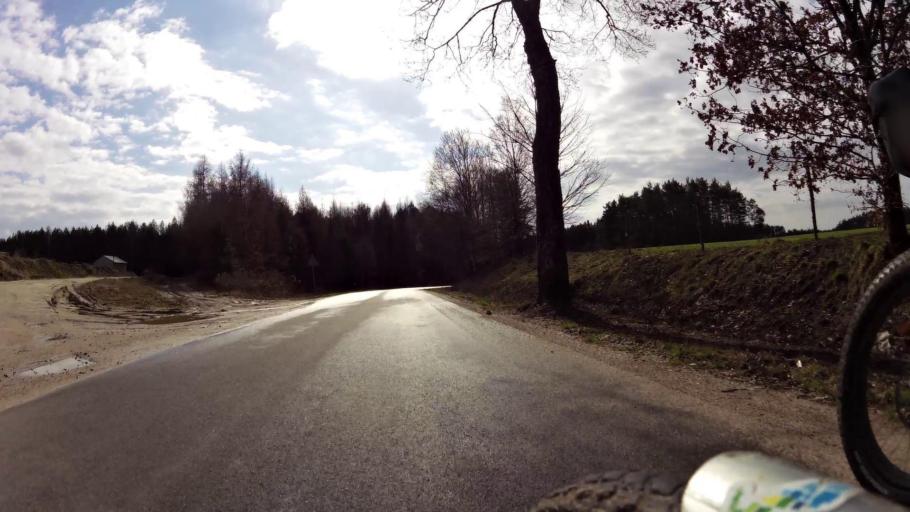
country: PL
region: Pomeranian Voivodeship
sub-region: Powiat bytowski
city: Kolczyglowy
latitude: 54.2080
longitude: 17.2355
